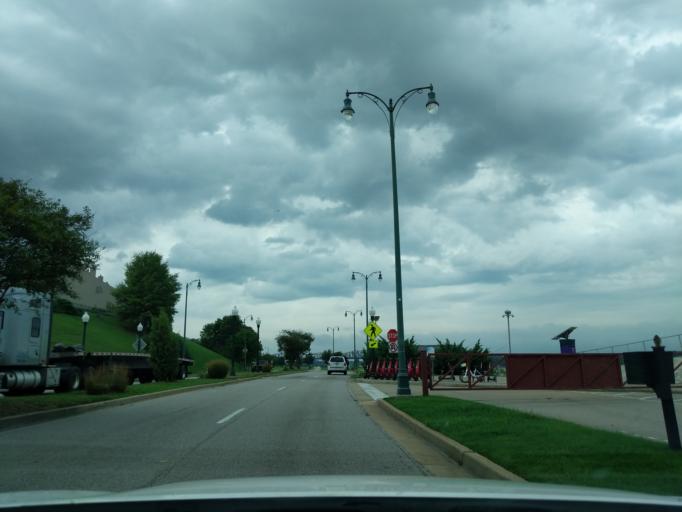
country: US
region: Tennessee
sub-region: Shelby County
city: Memphis
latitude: 35.1399
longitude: -90.0601
